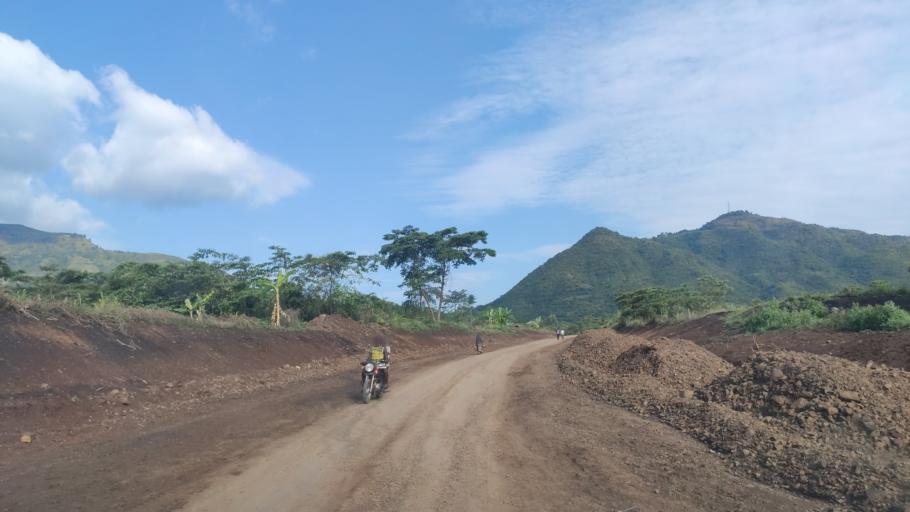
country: ET
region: Southern Nations, Nationalities, and People's Region
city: Arba Minch'
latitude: 6.4273
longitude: 37.3277
